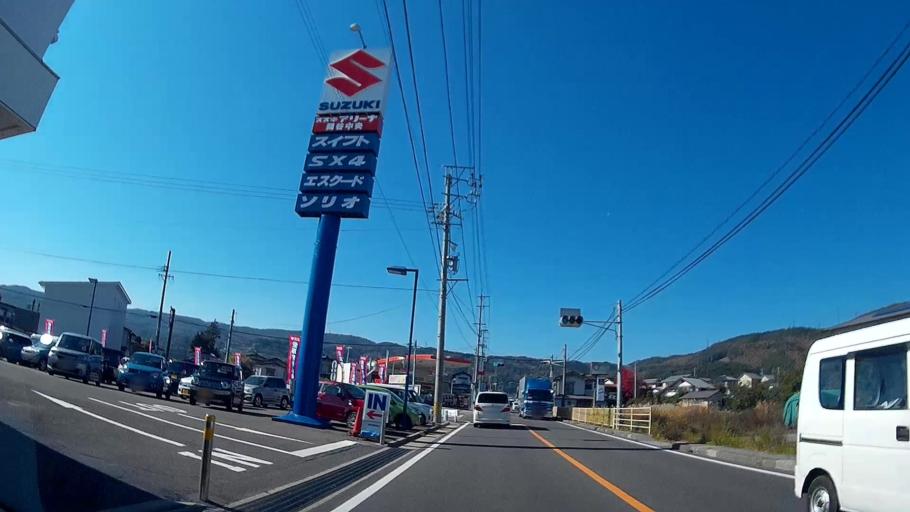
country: JP
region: Nagano
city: Okaya
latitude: 36.0809
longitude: 138.0522
